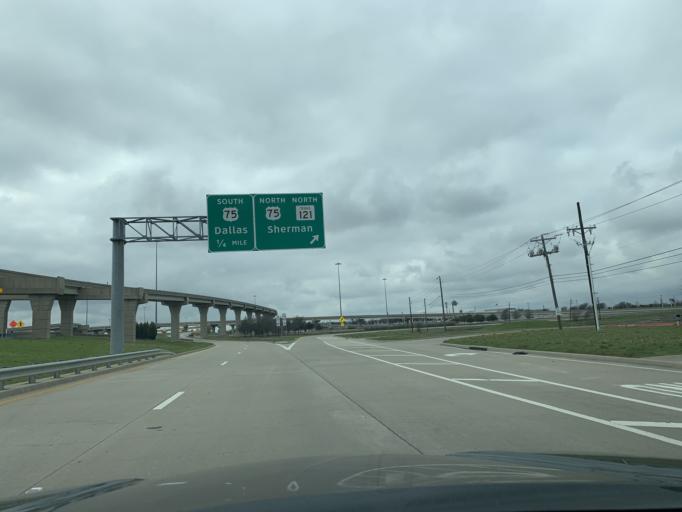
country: US
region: Texas
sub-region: Collin County
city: Fairview
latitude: 33.1612
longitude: -96.6402
